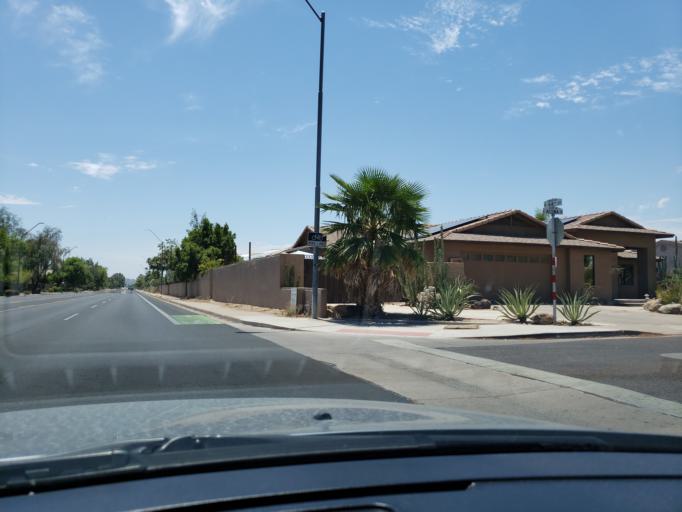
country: US
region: Arizona
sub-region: Maricopa County
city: Paradise Valley
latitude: 33.6184
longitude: -111.9434
